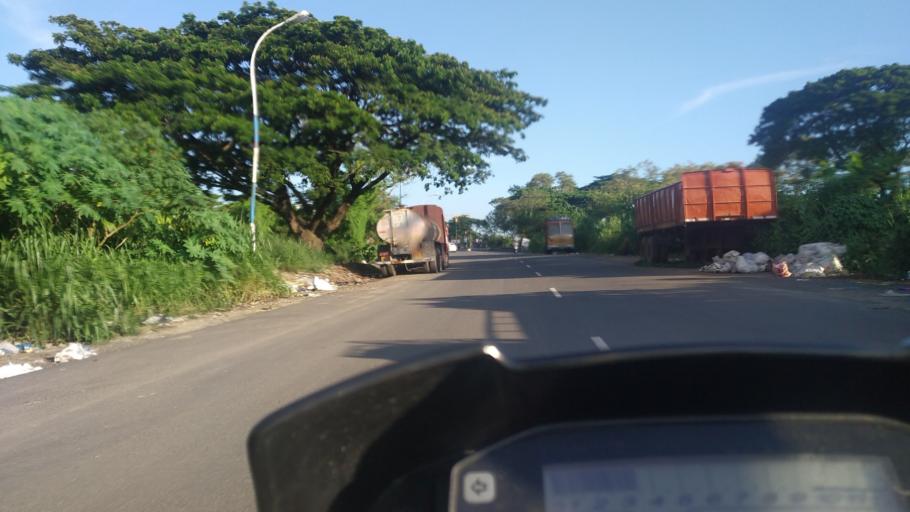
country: IN
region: Kerala
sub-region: Ernakulam
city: Cochin
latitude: 9.9367
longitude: 76.2707
